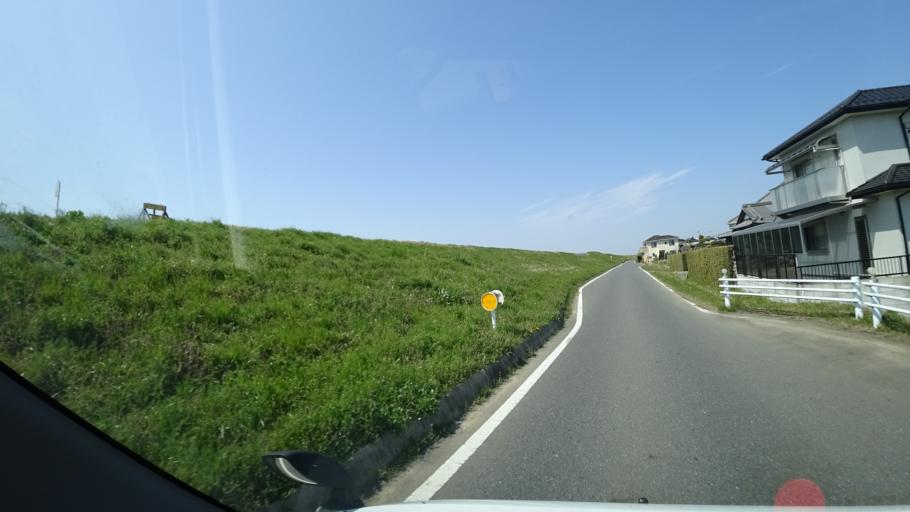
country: JP
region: Ibaraki
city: Edosaki
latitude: 35.8673
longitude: 140.3082
